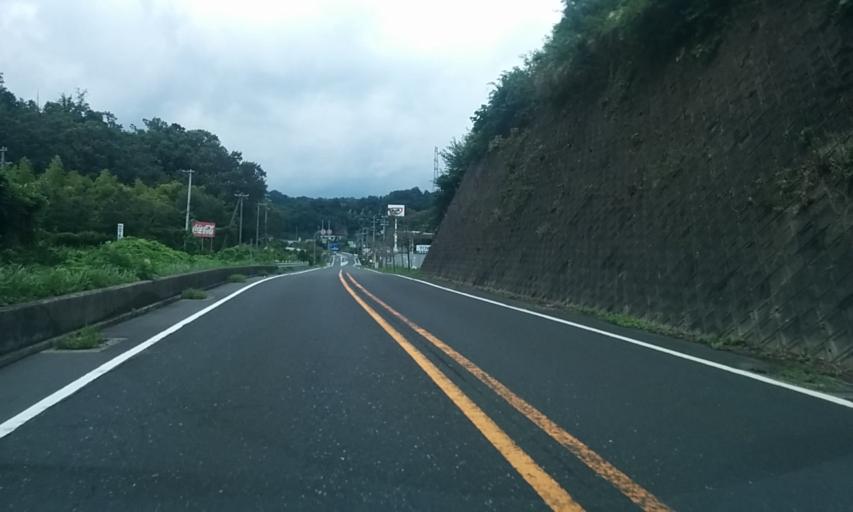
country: JP
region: Kyoto
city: Miyazu
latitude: 35.5491
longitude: 135.2312
